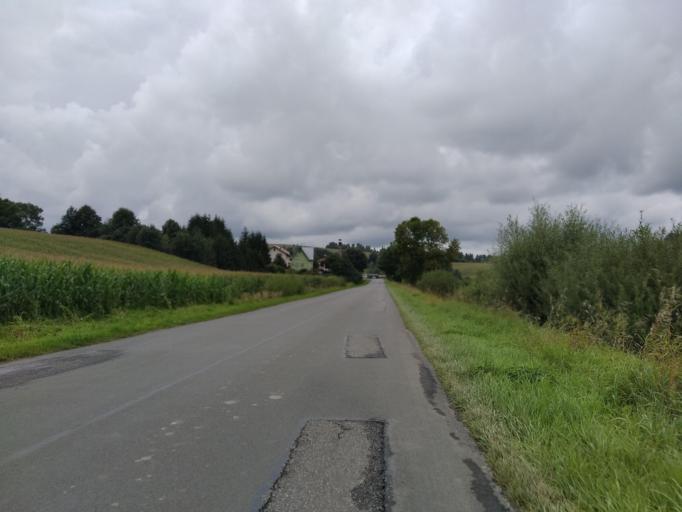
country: PL
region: Subcarpathian Voivodeship
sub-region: Powiat przemyski
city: Bircza
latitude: 49.7006
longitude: 22.3729
